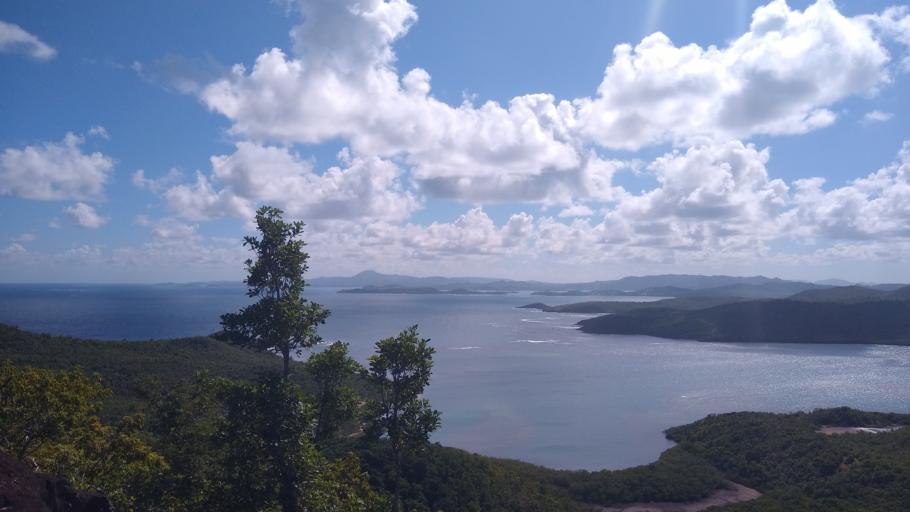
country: MQ
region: Martinique
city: Petite Riviere Salee
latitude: 14.7727
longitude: -60.8822
